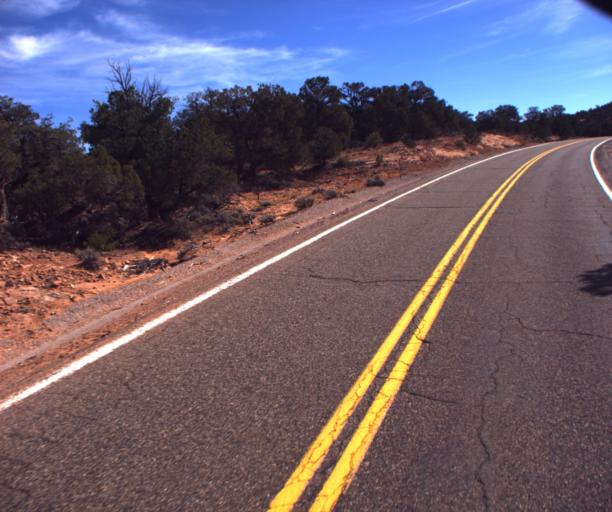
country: US
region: Arizona
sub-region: Navajo County
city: Kayenta
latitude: 36.6561
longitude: -110.5216
